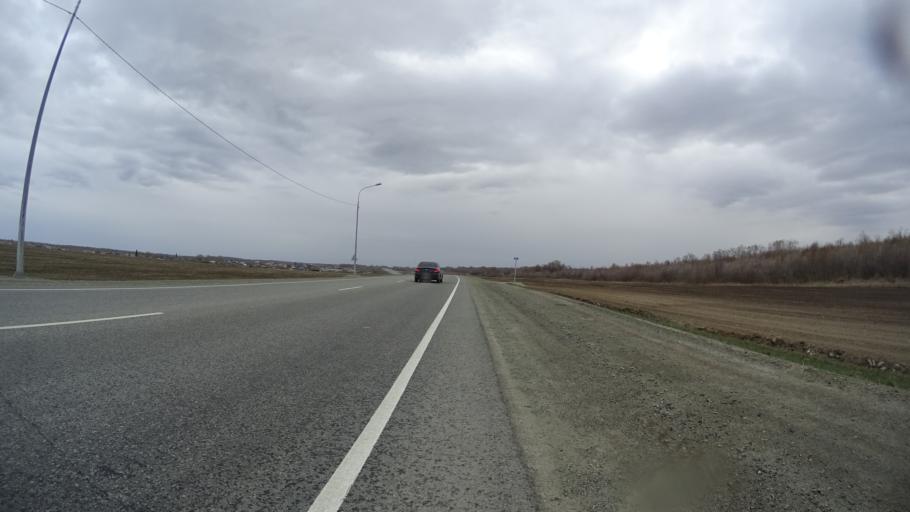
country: RU
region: Chelyabinsk
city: Krasnogorskiy
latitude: 54.6811
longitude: 61.2469
